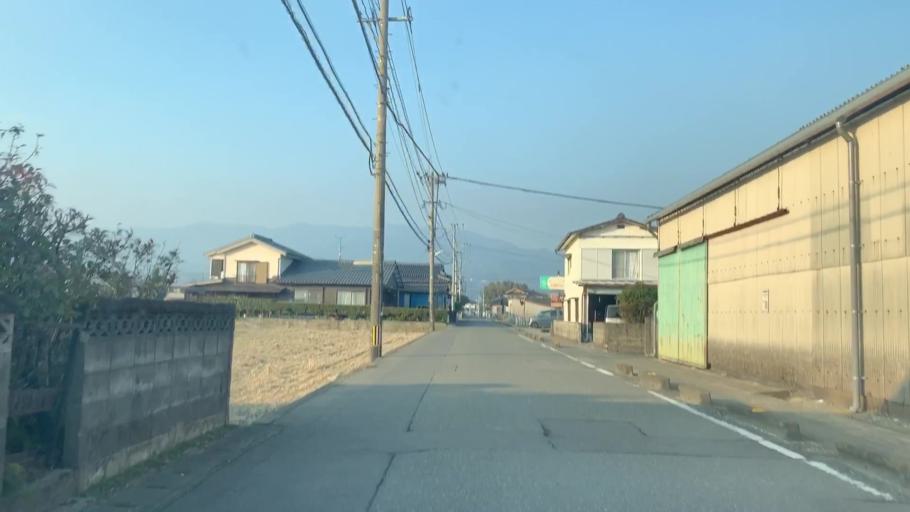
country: JP
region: Saga Prefecture
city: Saga-shi
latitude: 33.2775
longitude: 130.2265
